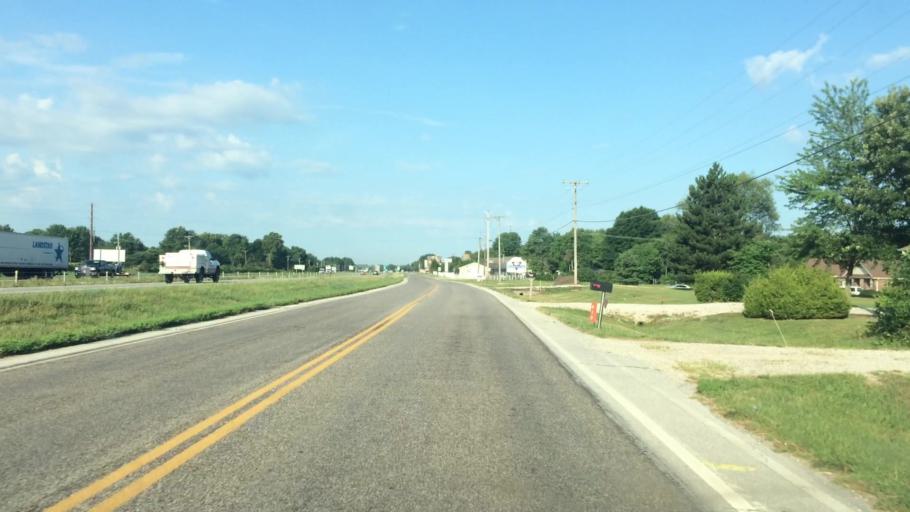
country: US
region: Missouri
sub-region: Greene County
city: Strafford
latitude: 37.2717
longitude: -93.1252
